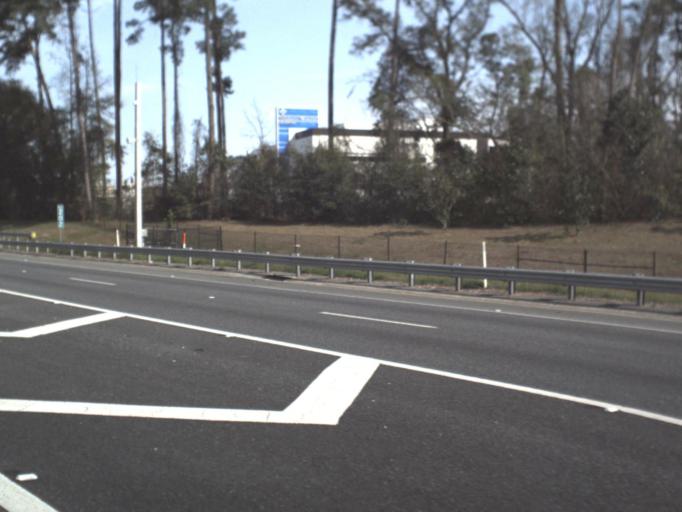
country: US
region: Florida
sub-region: Leon County
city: Tallahassee
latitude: 30.5009
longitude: -84.2588
